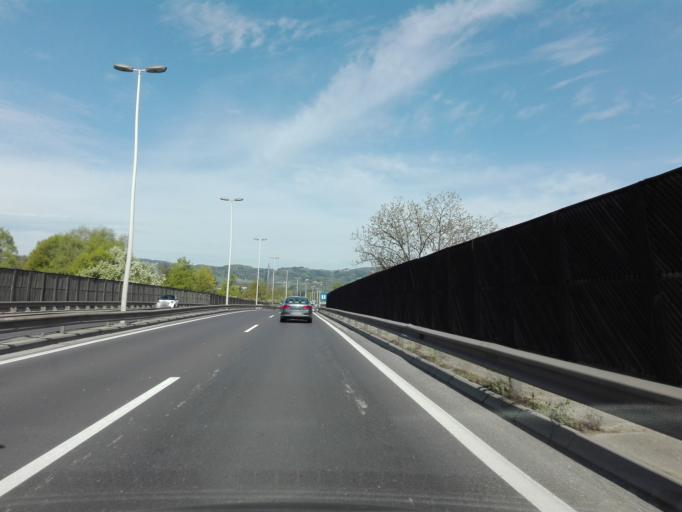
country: AT
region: Upper Austria
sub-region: Linz Stadt
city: Linz
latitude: 48.3133
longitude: 14.3086
